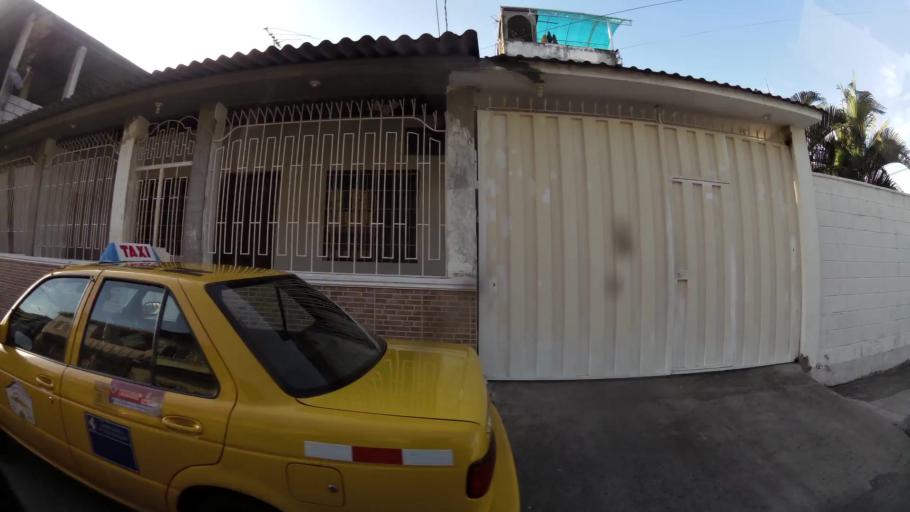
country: EC
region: Guayas
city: Guayaquil
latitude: -2.2276
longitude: -79.9071
